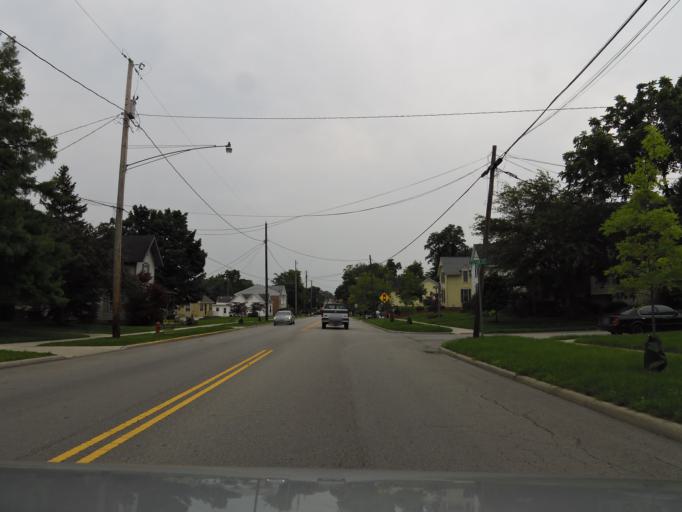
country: US
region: Ohio
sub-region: Clinton County
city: Wilmington
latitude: 39.4525
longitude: -83.8281
